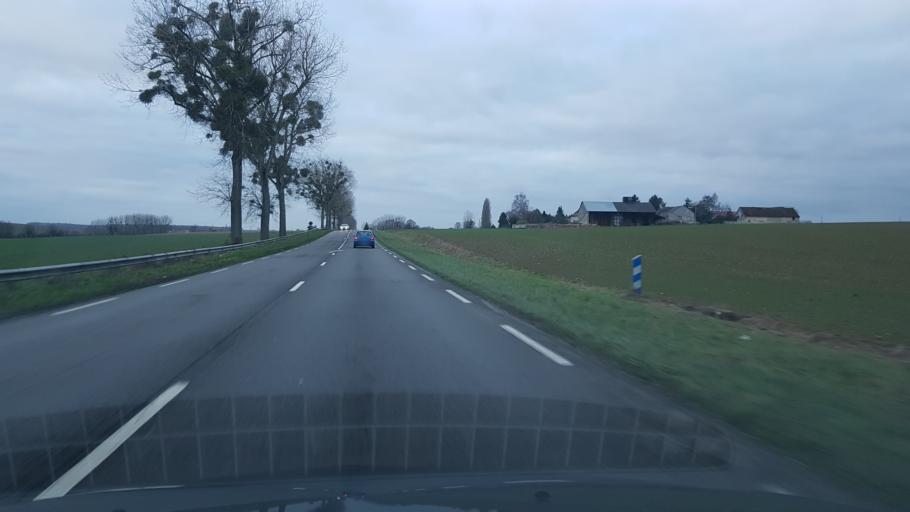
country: FR
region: Ile-de-France
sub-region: Departement de Seine-et-Marne
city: La Ferte-Gaucher
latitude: 48.6936
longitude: 3.3191
